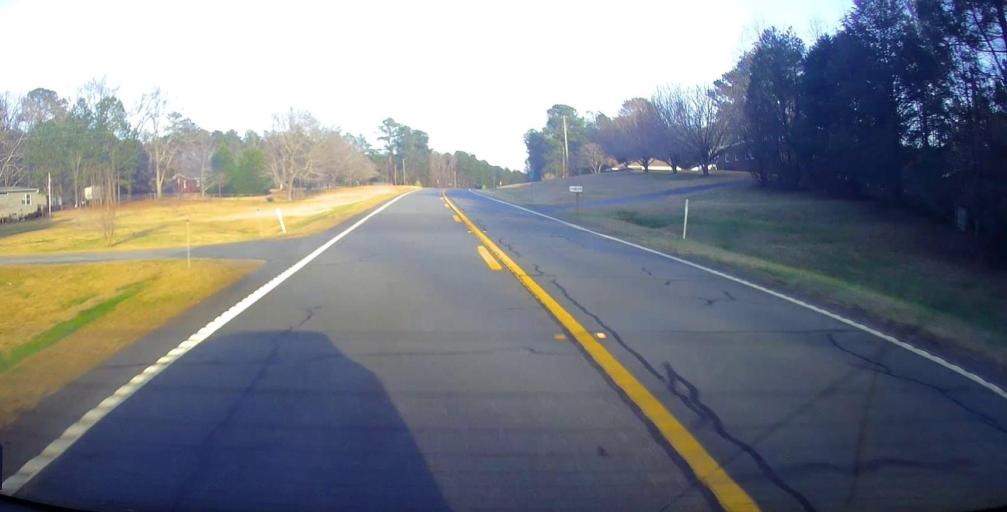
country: US
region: Georgia
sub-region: Talbot County
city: Sardis
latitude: 32.7922
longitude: -84.5443
